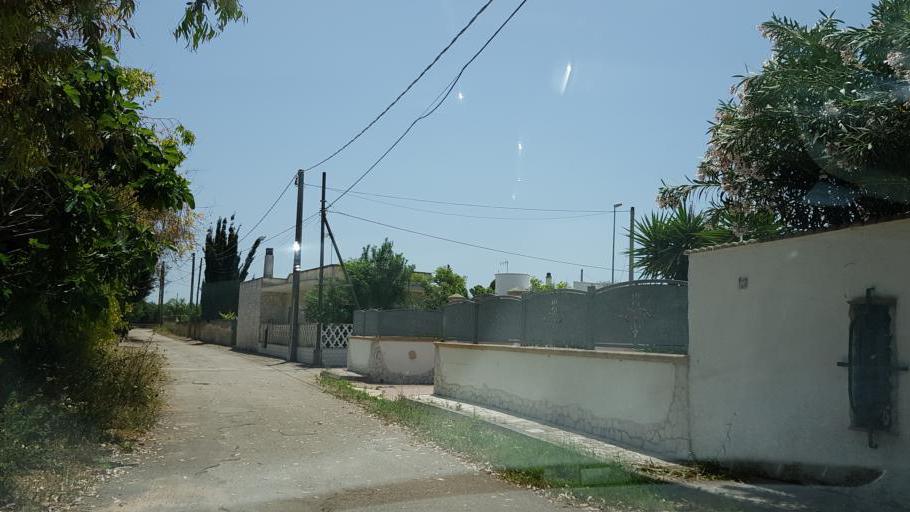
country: IT
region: Apulia
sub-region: Provincia di Lecce
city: Porto Cesareo
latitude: 40.2489
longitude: 17.9227
